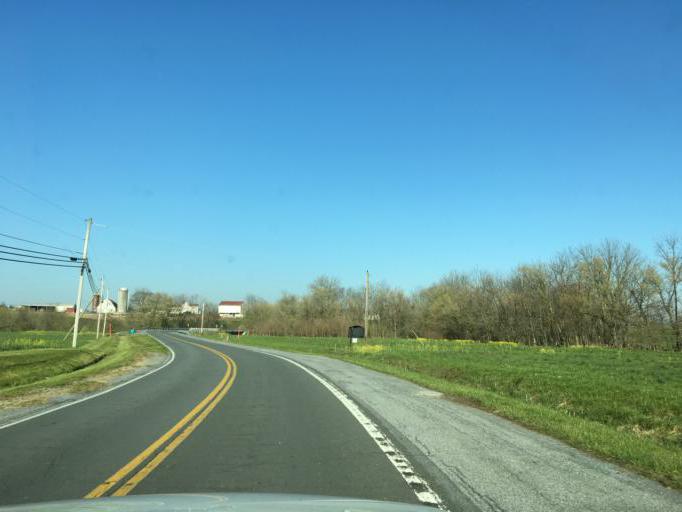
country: US
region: Maryland
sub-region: Frederick County
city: Walkersville
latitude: 39.4932
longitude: -77.3212
